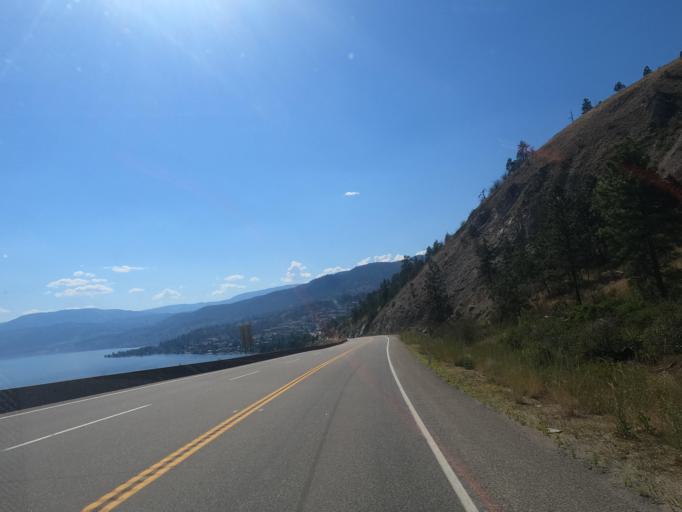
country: CA
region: British Columbia
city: Peachland
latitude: 49.7985
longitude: -119.6817
